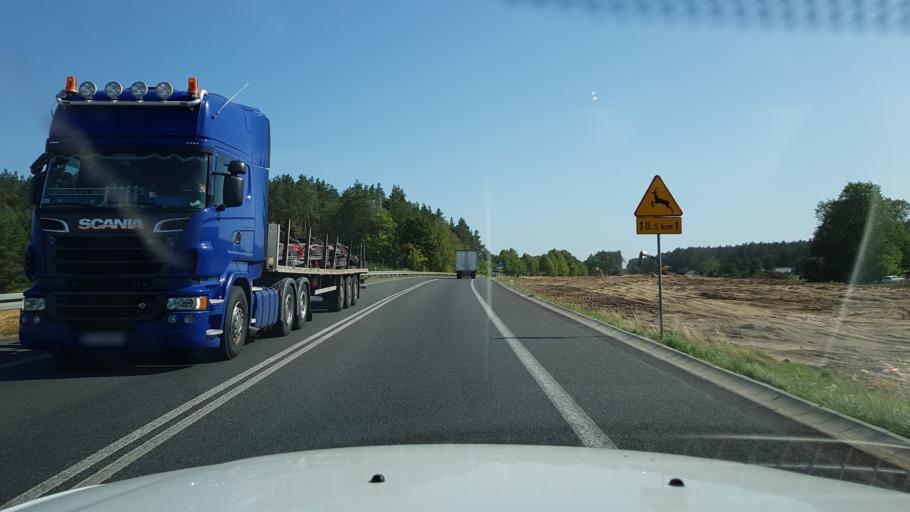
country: PL
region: West Pomeranian Voivodeship
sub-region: Powiat goleniowski
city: Przybiernow
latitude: 53.7452
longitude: 14.7753
